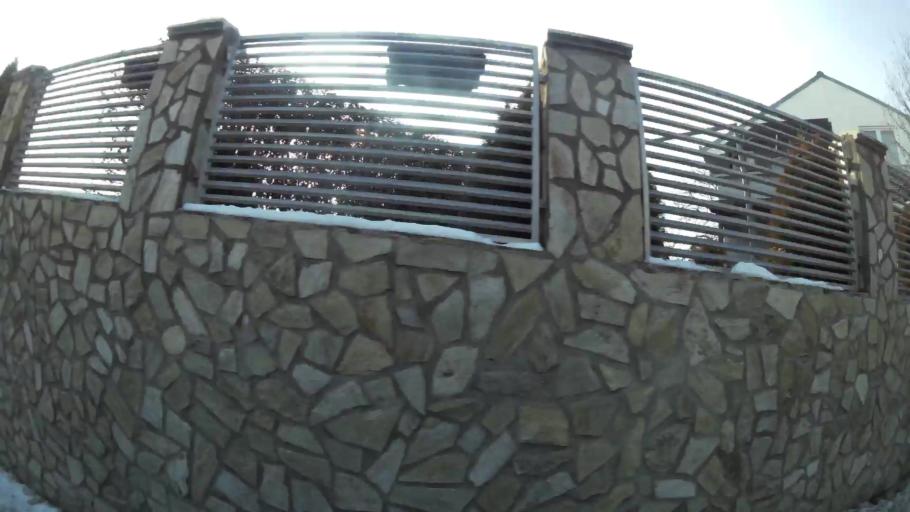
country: MK
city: Creshevo
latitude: 42.0136
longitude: 21.5042
